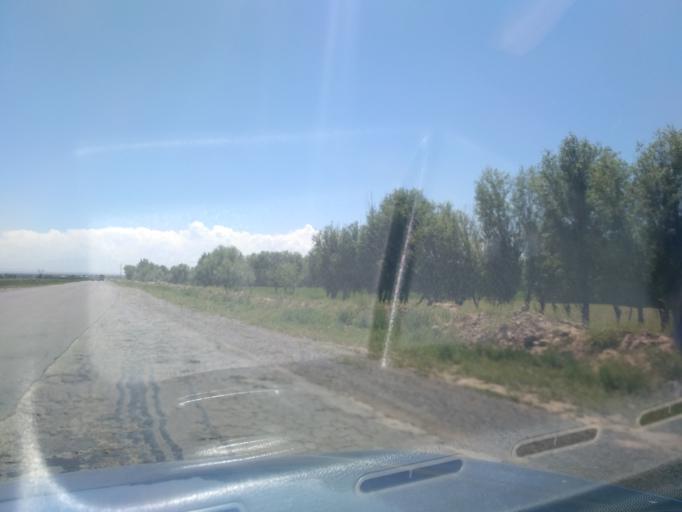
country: UZ
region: Sirdaryo
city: Yangiyer
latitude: 40.2323
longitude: 68.8471
